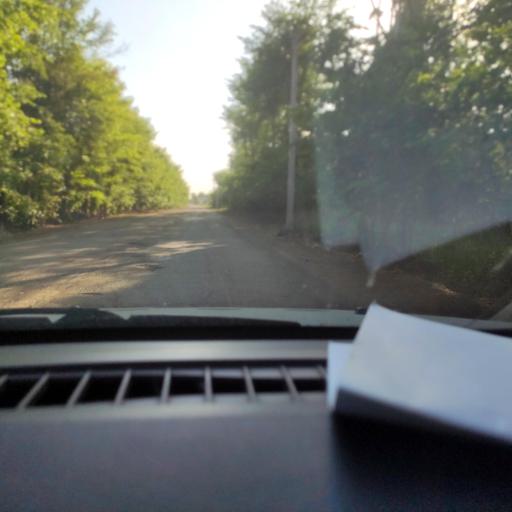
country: RU
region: Perm
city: Krasnokamsk
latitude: 58.1401
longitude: 55.6904
